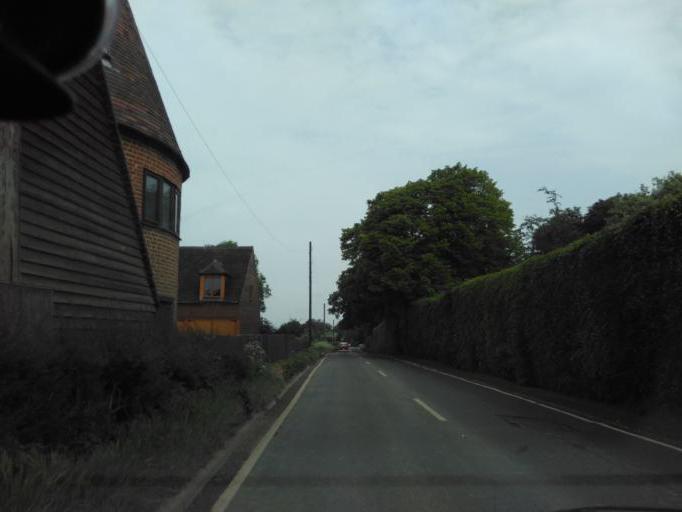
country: GB
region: England
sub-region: Kent
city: Chartham
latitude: 51.1951
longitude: 1.0560
